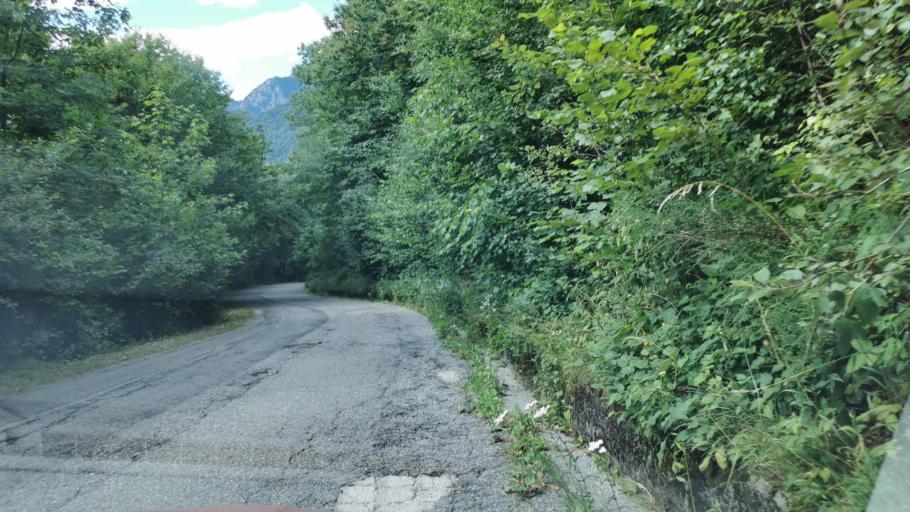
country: IT
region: Lombardy
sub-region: Provincia di Lecco
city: Casargo
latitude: 46.0450
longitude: 9.3956
